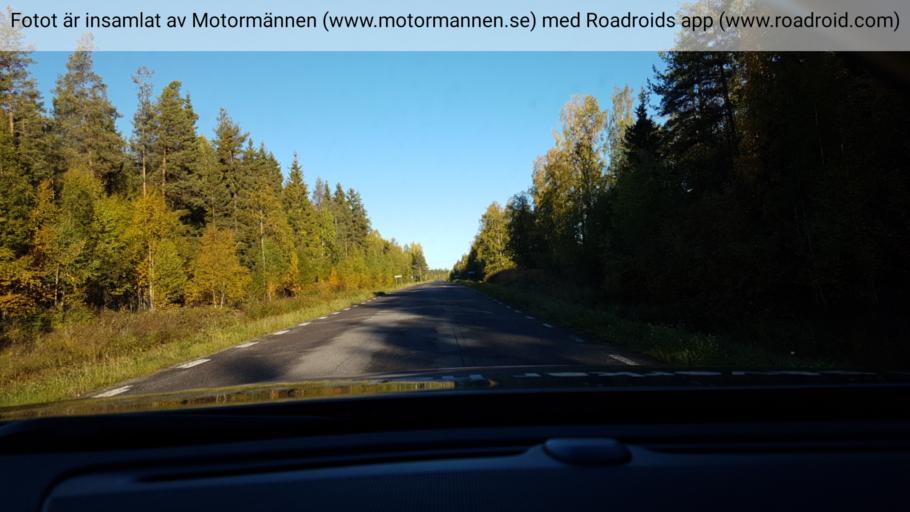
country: SE
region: Norrbotten
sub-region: Bodens Kommun
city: Boden
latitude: 66.0613
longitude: 21.4106
